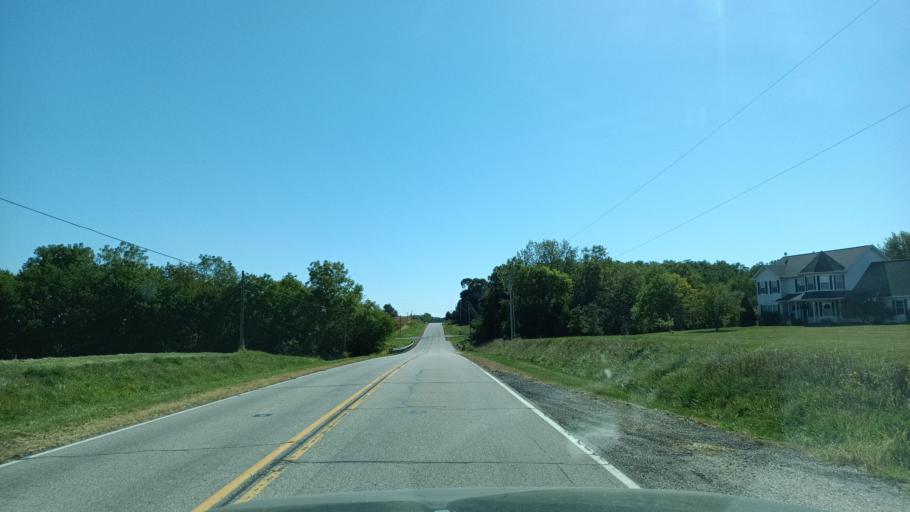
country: US
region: Illinois
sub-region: Peoria County
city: Elmwood
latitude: 40.8479
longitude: -89.9106
